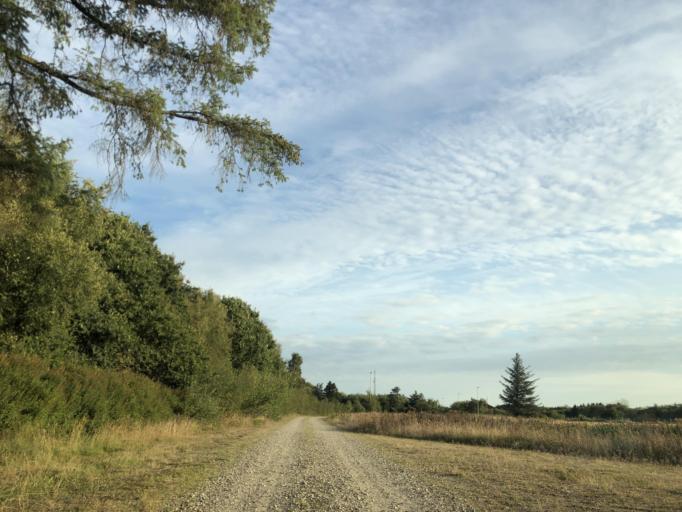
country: DK
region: Central Jutland
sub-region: Holstebro Kommune
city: Ulfborg
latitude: 56.2580
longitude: 8.3209
